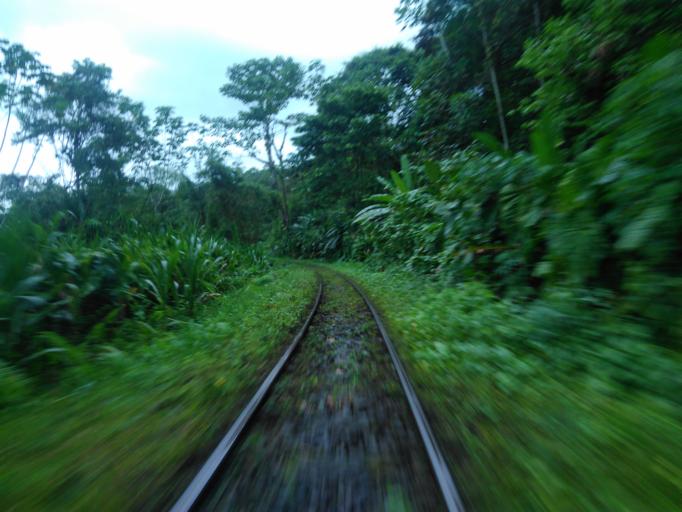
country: CO
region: Valle del Cauca
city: Buenaventura
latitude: 3.8400
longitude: -76.8715
